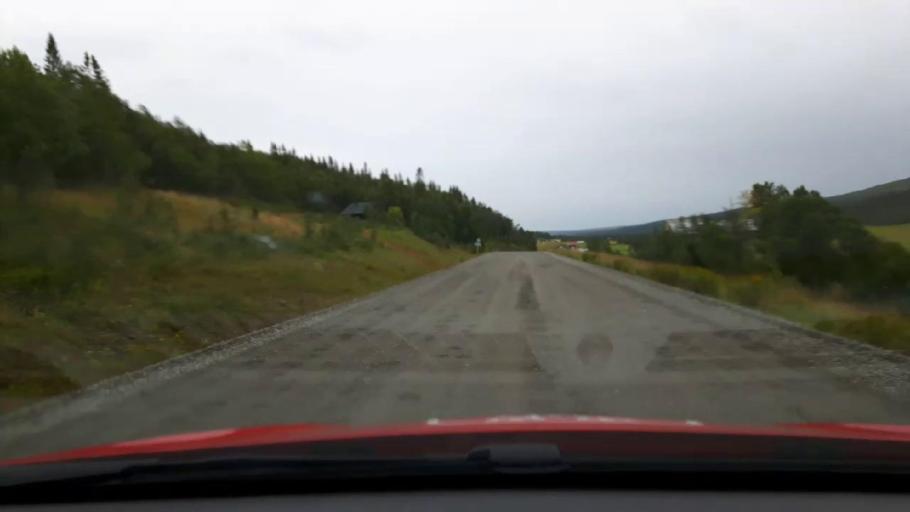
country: NO
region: Nord-Trondelag
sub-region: Meraker
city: Meraker
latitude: 63.5325
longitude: 12.3898
